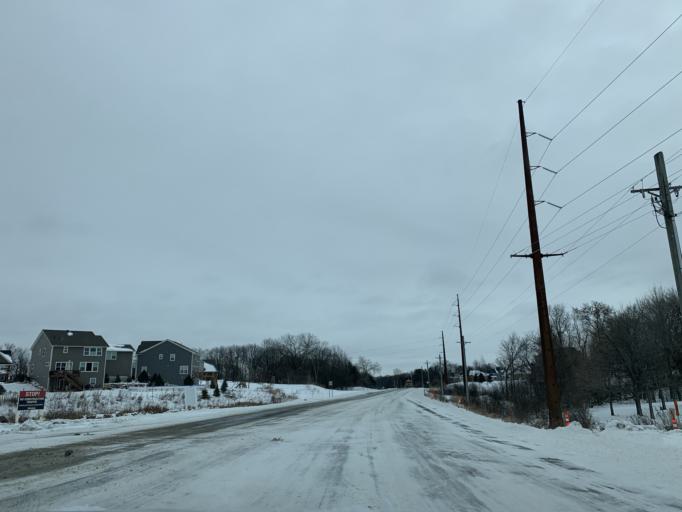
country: US
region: Minnesota
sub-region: Carver County
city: Chaska
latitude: 44.7901
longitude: -93.6219
